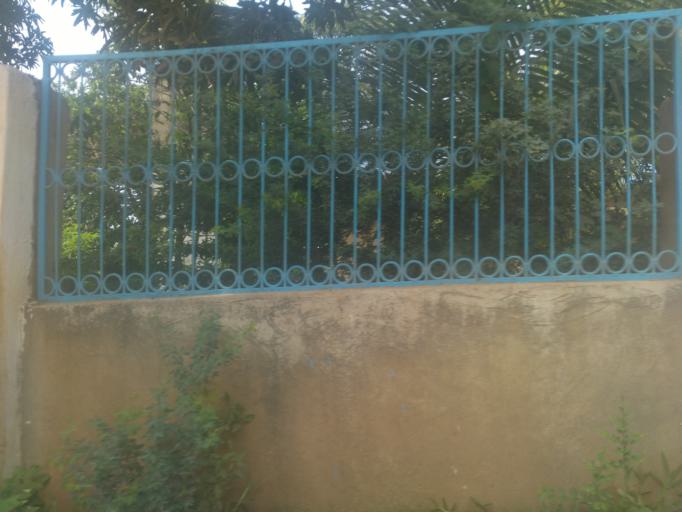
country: TZ
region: Zanzibar Urban/West
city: Zanzibar
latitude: -6.2320
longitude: 39.2192
